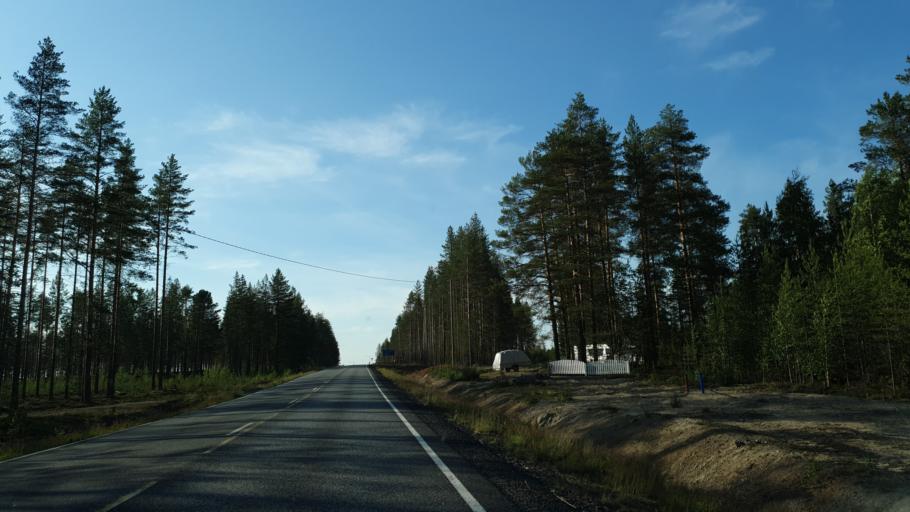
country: FI
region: Kainuu
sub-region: Kehys-Kainuu
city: Kuhmo
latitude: 64.0949
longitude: 29.4779
